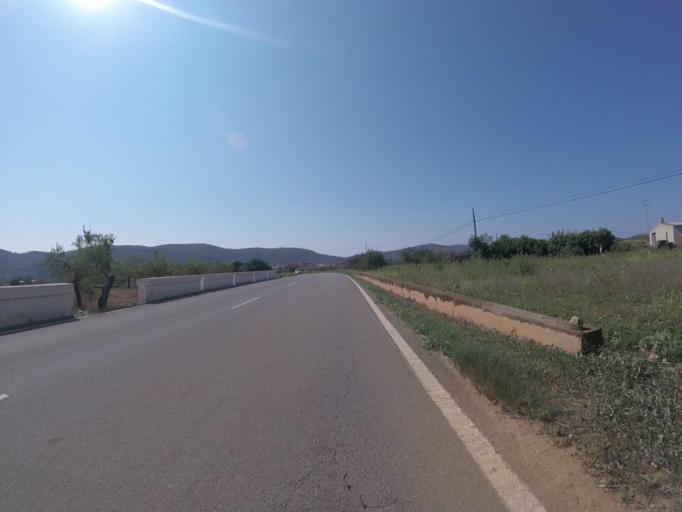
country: ES
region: Valencia
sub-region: Provincia de Castello
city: Adzaneta
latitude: 40.2246
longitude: -0.1732
